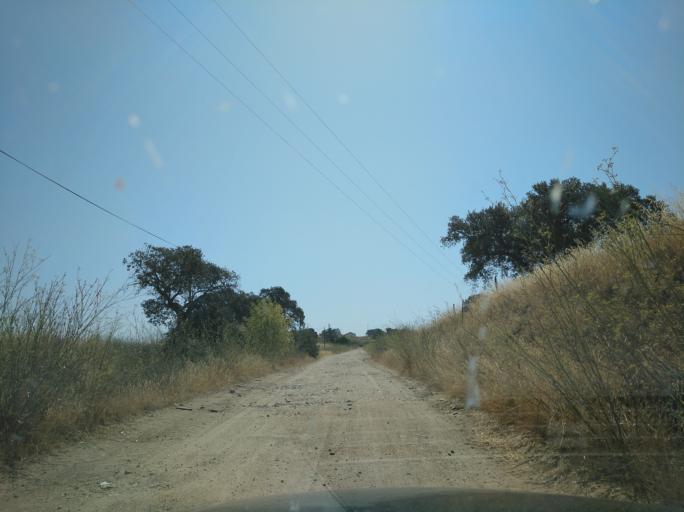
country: PT
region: Portalegre
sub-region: Campo Maior
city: Campo Maior
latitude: 39.0319
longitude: -6.9816
